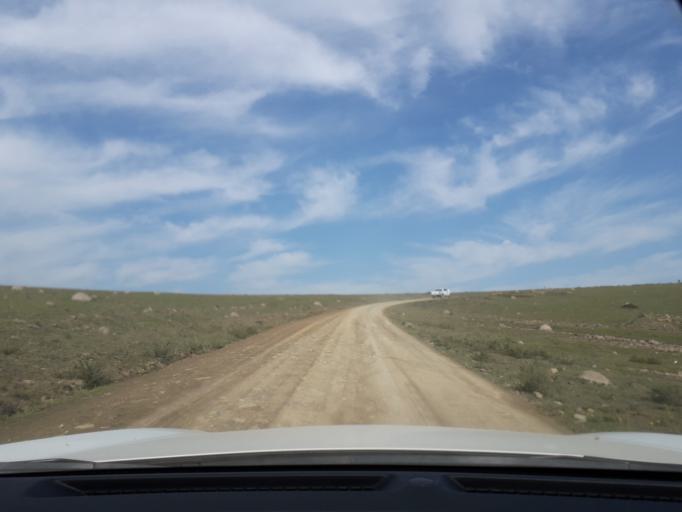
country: ZA
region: Eastern Cape
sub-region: Buffalo City Metropolitan Municipality
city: Bhisho
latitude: -33.0042
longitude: 27.3169
